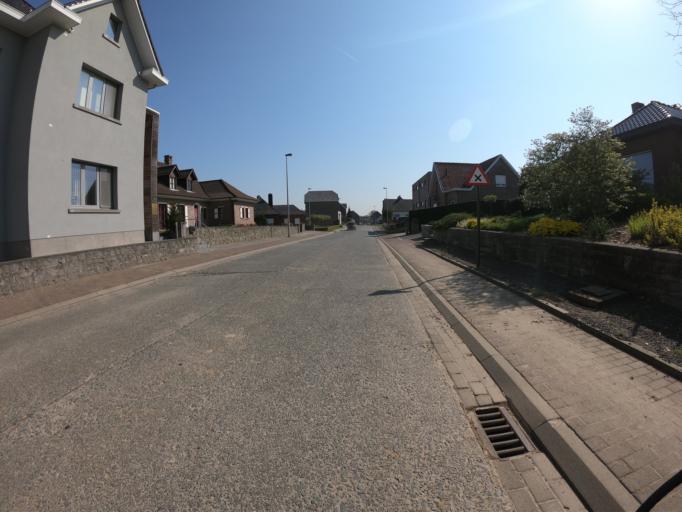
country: BE
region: Wallonia
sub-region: Province du Hainaut
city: Lessines
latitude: 50.7617
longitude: 3.8213
